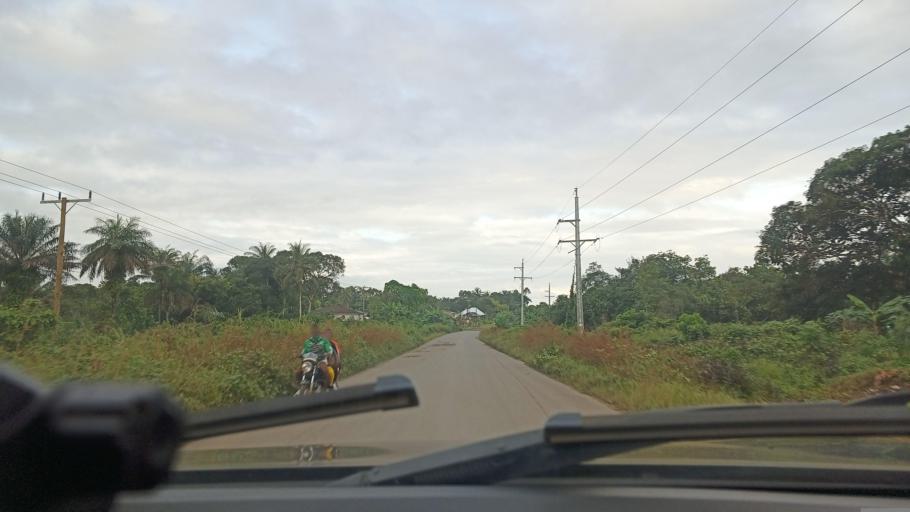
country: LR
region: Montserrado
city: Monrovia
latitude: 6.5618
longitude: -10.8714
